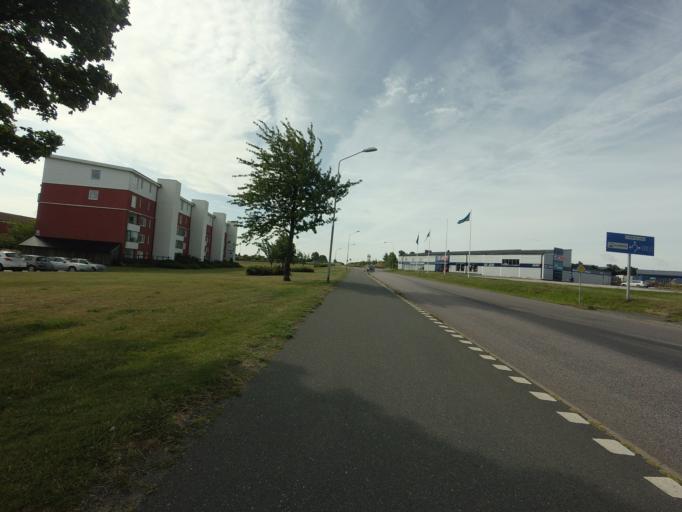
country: SE
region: Skane
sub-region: Simrishamns Kommun
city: Simrishamn
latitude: 55.5513
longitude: 14.3490
